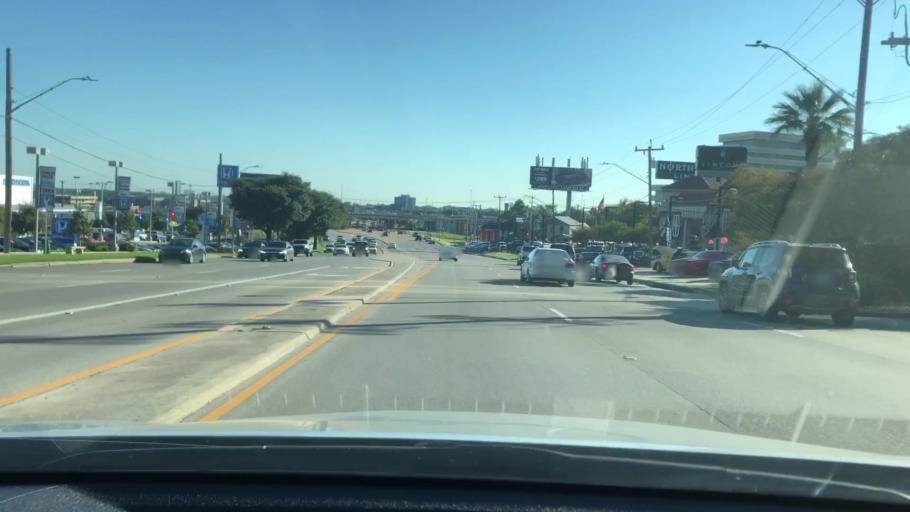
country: US
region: Texas
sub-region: Bexar County
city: Castle Hills
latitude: 29.5251
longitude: -98.4991
